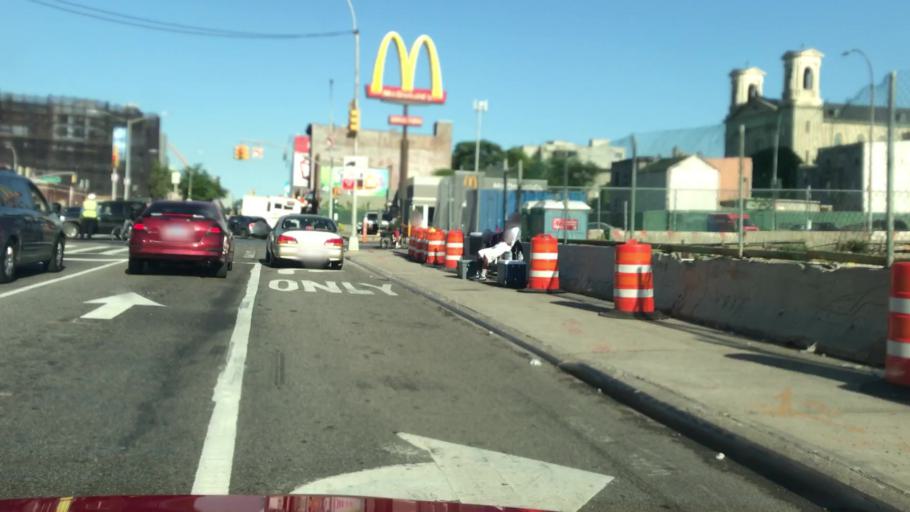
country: US
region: New York
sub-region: Kings County
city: Brooklyn
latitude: 40.6817
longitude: -73.9680
